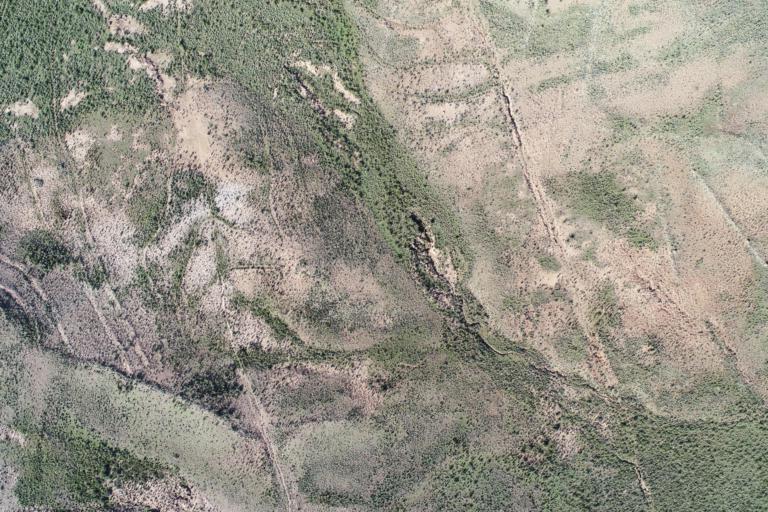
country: BO
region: La Paz
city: Curahuara de Carangas
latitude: -17.3045
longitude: -68.5031
